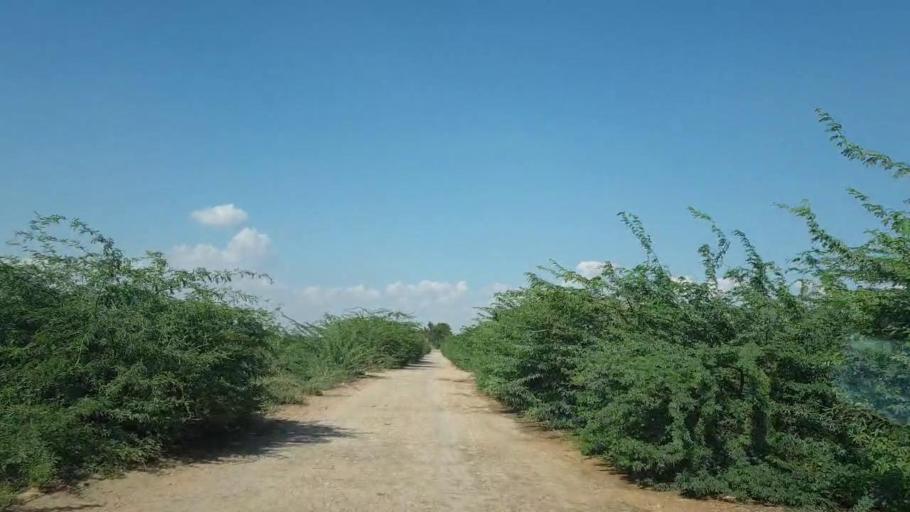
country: PK
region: Sindh
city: Pithoro
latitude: 25.6382
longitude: 69.4424
